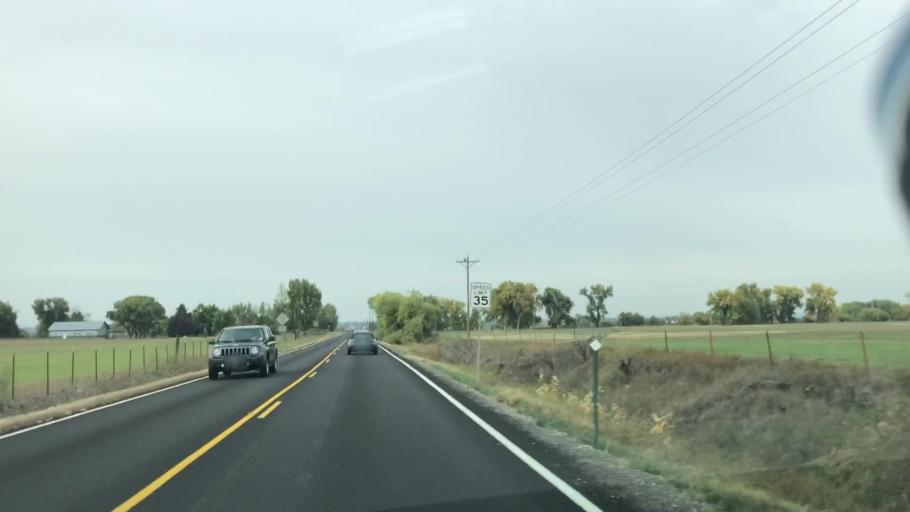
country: US
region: Colorado
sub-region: Larimer County
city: Loveland
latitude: 40.4687
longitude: -105.0584
